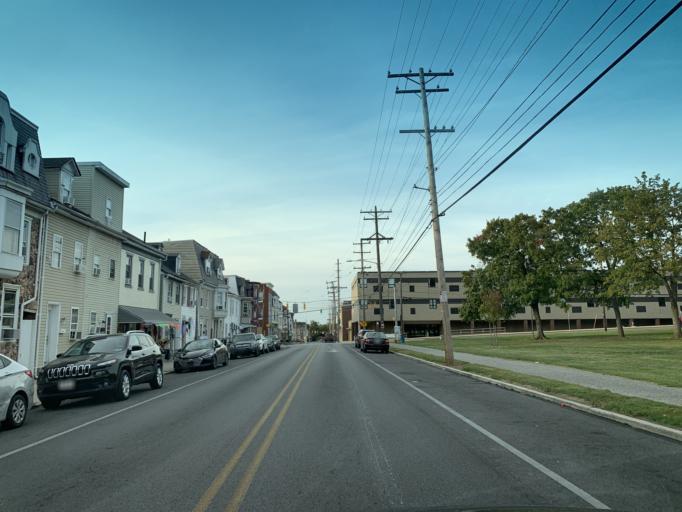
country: US
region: Pennsylvania
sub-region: York County
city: York
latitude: 39.9564
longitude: -76.7291
